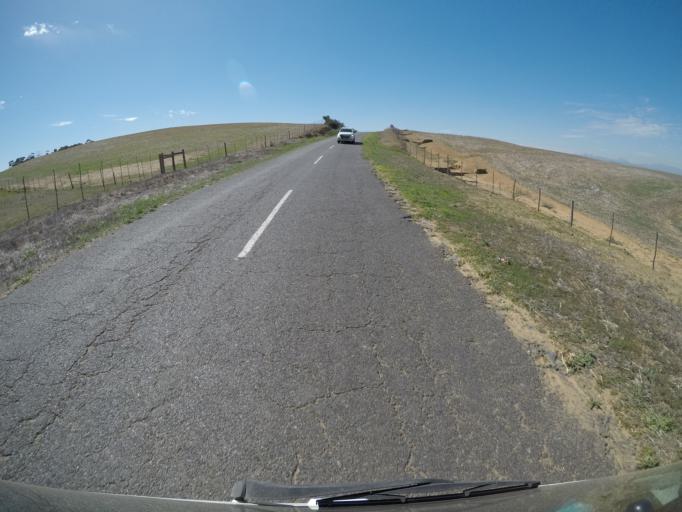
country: ZA
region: Western Cape
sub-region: City of Cape Town
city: Sunset Beach
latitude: -33.7427
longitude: 18.5614
